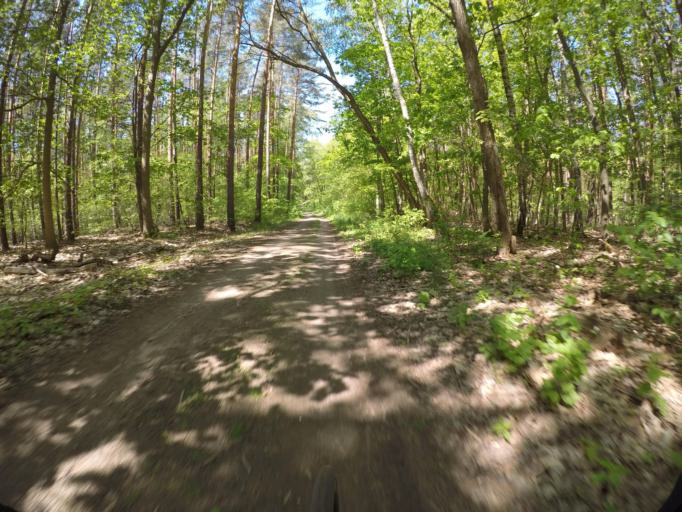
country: DE
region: Brandenburg
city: Potsdam
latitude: 52.4550
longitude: 13.0771
